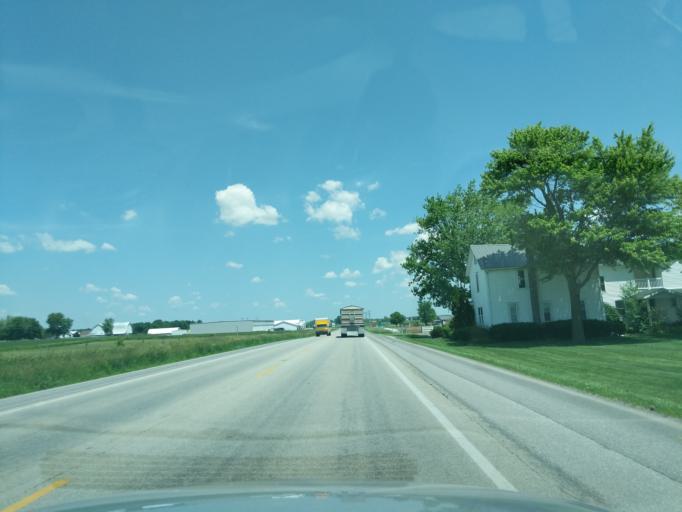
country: US
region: Indiana
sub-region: LaGrange County
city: Topeka
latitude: 41.5792
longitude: -85.5786
